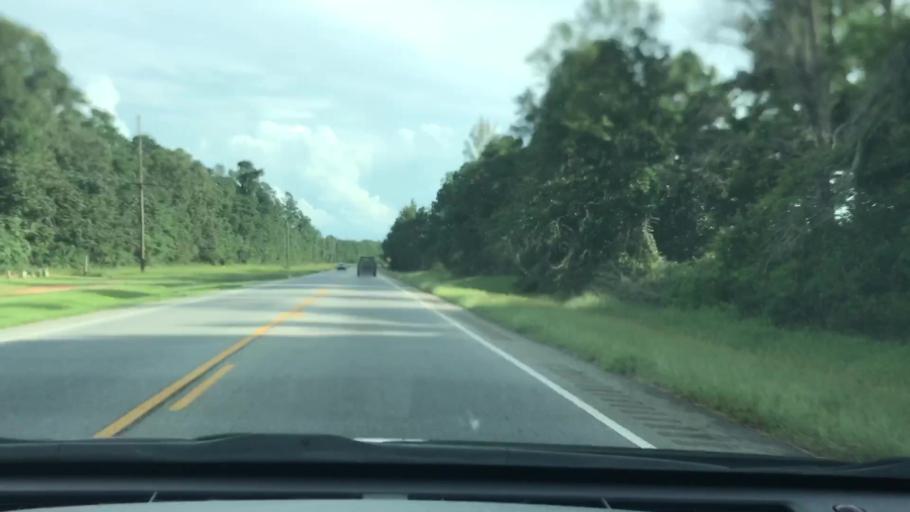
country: US
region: Georgia
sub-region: Jefferson County
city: Louisville
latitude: 33.0596
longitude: -82.4061
